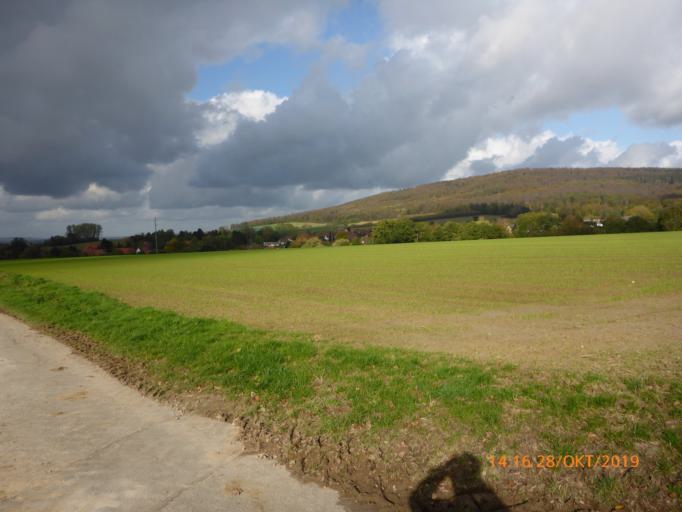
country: DE
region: Lower Saxony
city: Messenkamp
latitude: 52.2787
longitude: 9.3900
